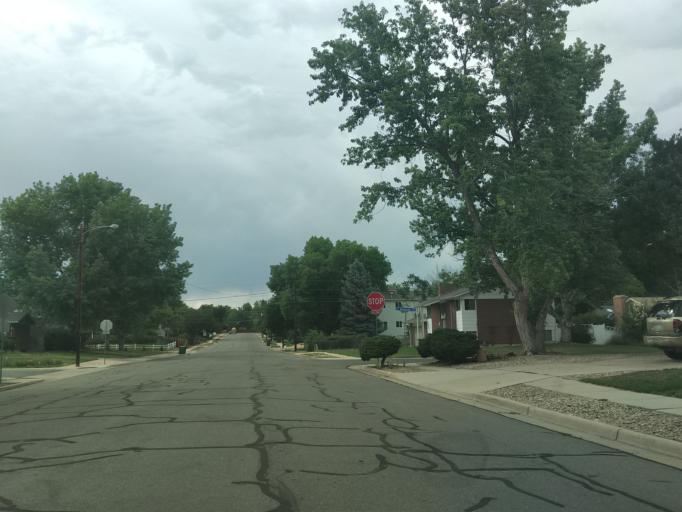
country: US
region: Colorado
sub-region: Jefferson County
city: Lakewood
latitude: 39.6977
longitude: -105.1046
